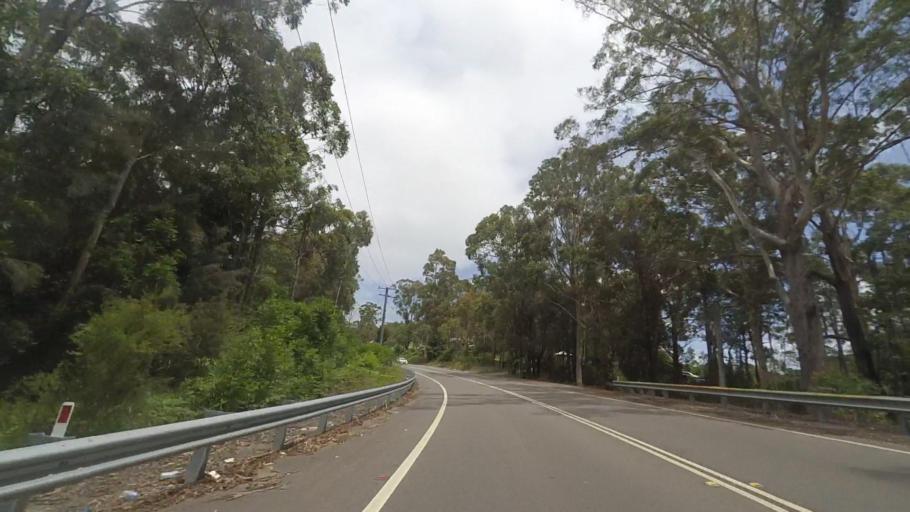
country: AU
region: New South Wales
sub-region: Wyong Shire
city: Chittaway Bay
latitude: -33.3317
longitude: 151.4113
